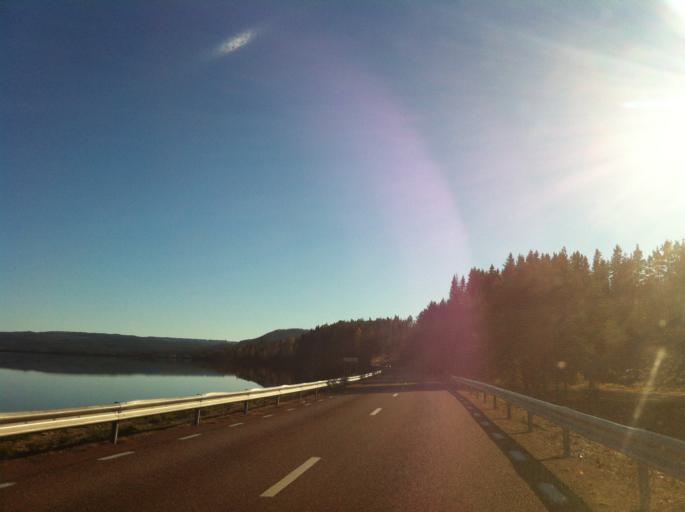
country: SE
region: Dalarna
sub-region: Alvdalens Kommun
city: AElvdalen
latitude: 61.3095
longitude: 13.6979
